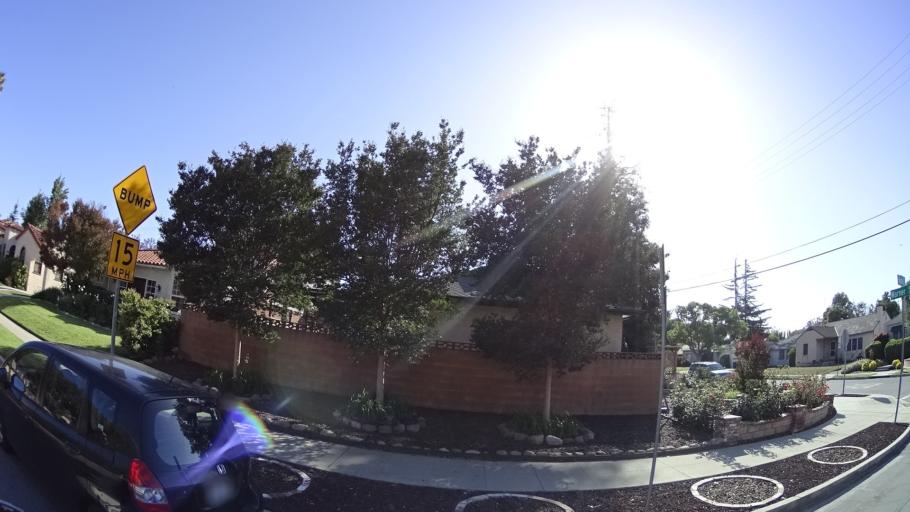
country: US
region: California
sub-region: Los Angeles County
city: Universal City
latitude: 34.1484
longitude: -118.3447
